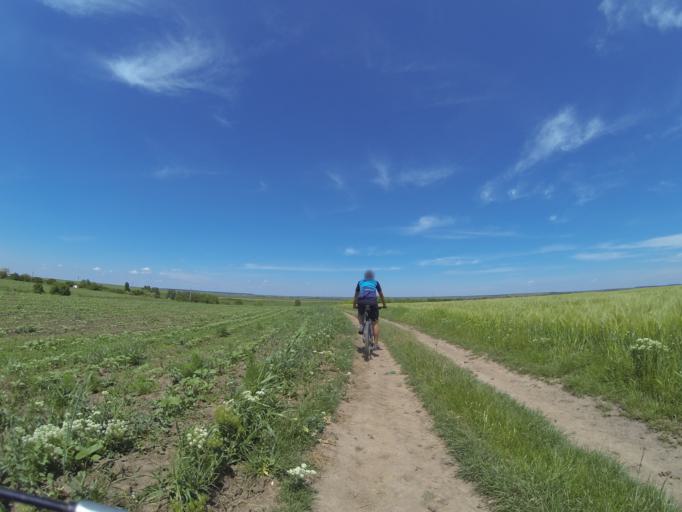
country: RO
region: Dolj
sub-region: Comuna Teslui
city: Teslui
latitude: 44.1977
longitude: 24.1409
